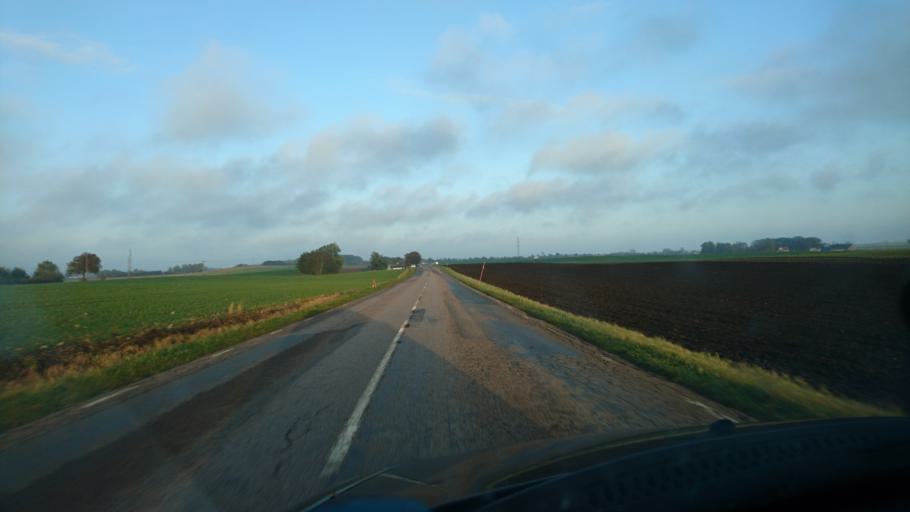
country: SE
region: Skane
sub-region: Tomelilla Kommun
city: Tomelilla
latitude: 55.4521
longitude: 14.1519
